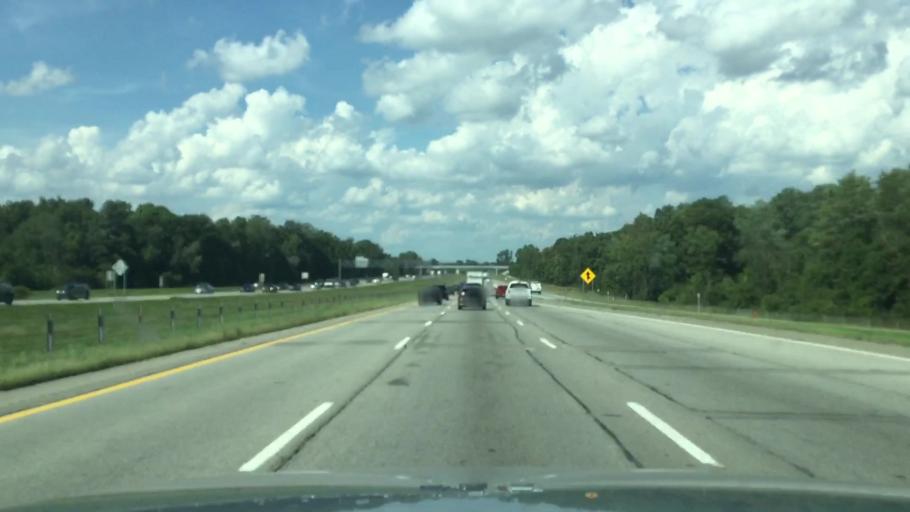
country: US
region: Michigan
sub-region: Wayne County
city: Canton
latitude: 42.3243
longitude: -83.4430
